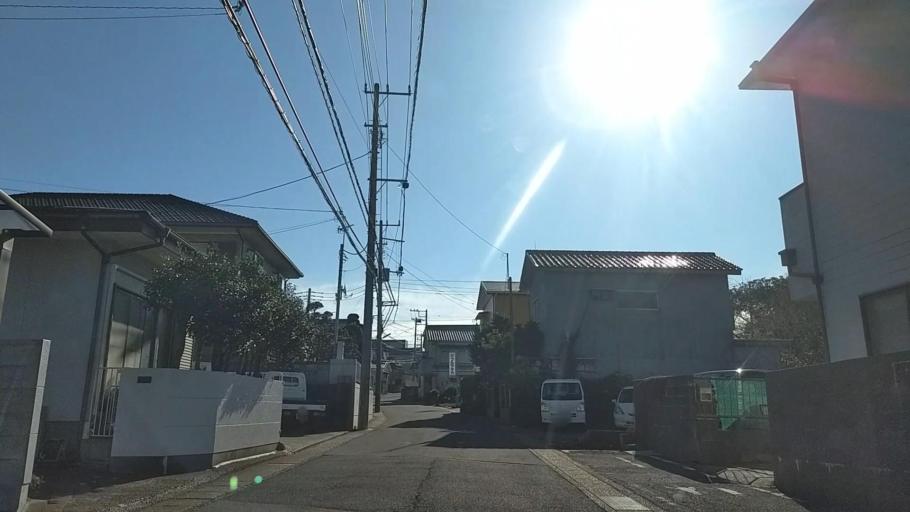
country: JP
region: Chiba
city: Hasaki
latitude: 35.7260
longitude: 140.8405
